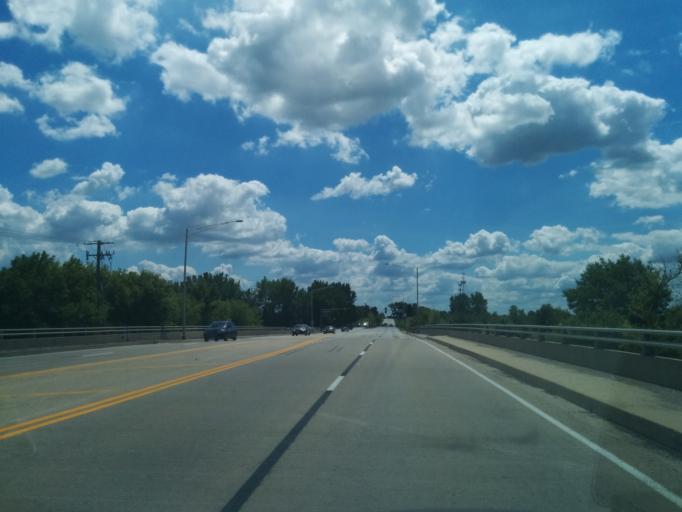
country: US
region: Illinois
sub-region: Will County
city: Plainfield
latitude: 41.6907
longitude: -88.1664
